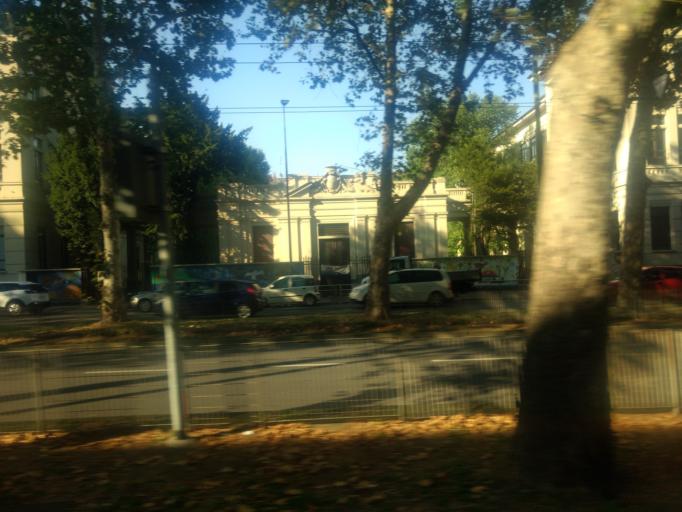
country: IT
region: Lombardy
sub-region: Citta metropolitana di Milano
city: Milano
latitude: 45.4976
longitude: 9.1682
